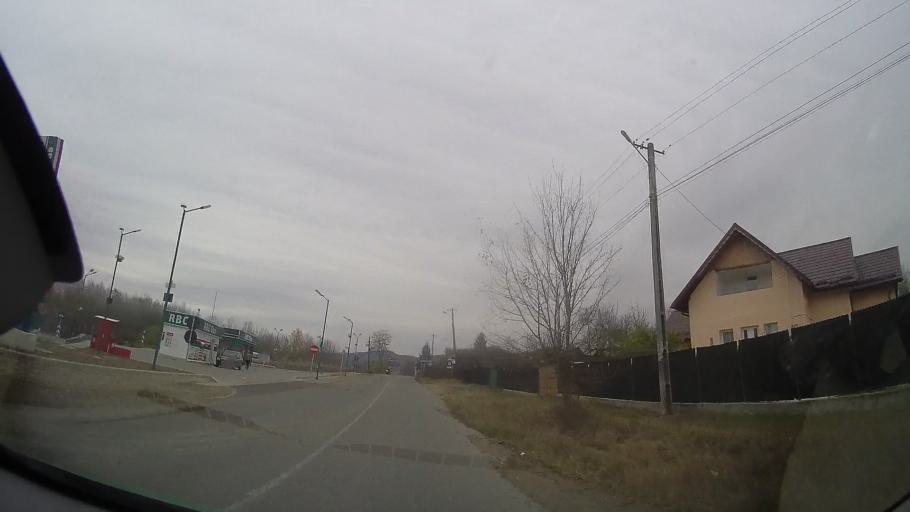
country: RO
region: Prahova
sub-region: Comuna Iordachianu
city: Iordacheanu
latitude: 45.0172
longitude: 26.2306
